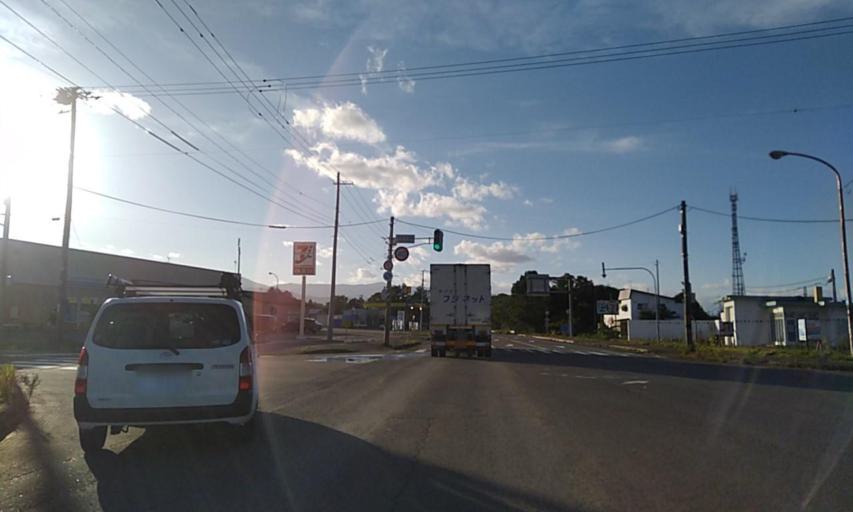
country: JP
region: Hokkaido
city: Otofuke
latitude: 42.9469
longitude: 142.9408
